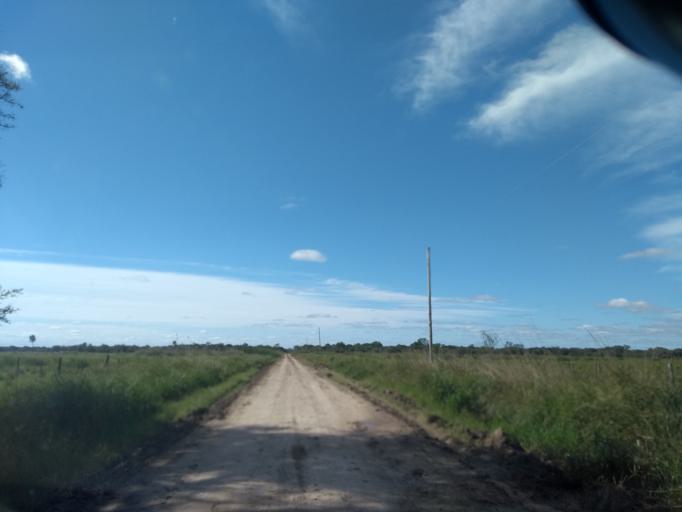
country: AR
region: Chaco
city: Colonia Benitez
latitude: -27.2900
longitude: -58.9346
